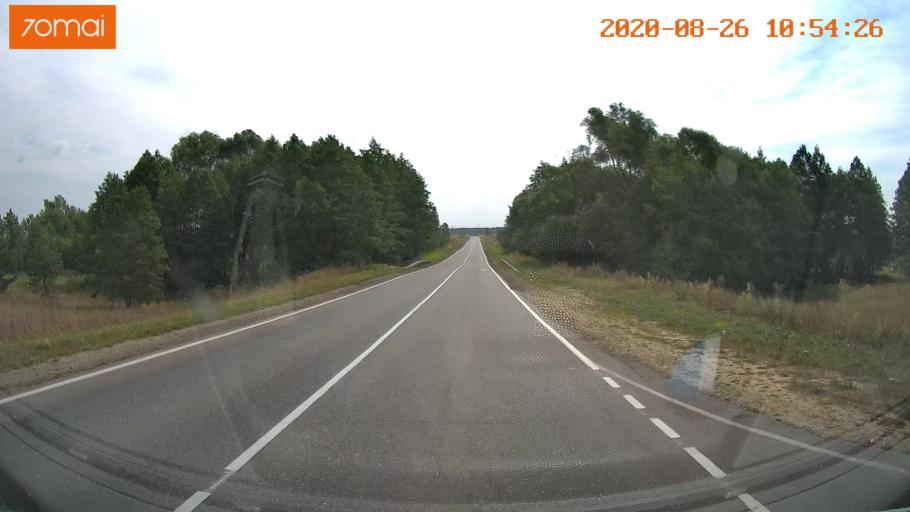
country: RU
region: Rjazan
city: Izhevskoye
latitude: 54.6287
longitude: 41.1616
